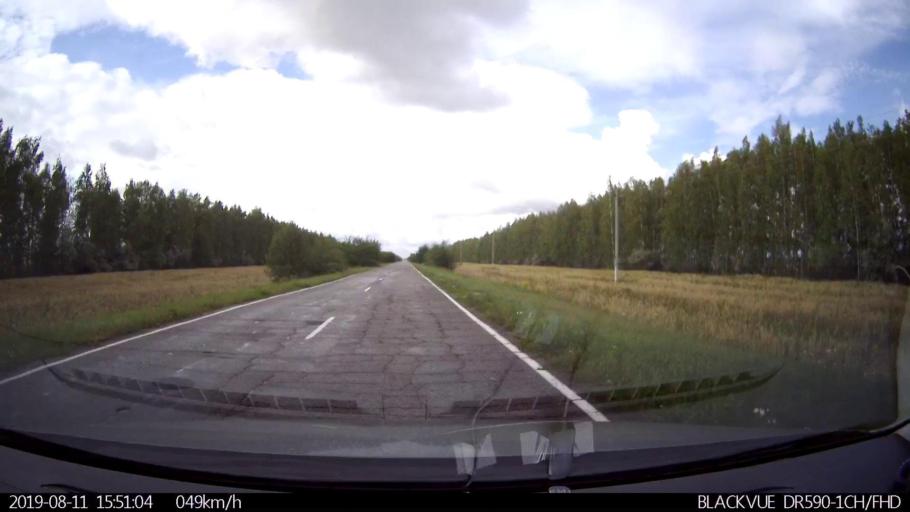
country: RU
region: Ulyanovsk
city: Ignatovka
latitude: 53.9159
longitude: 47.6559
